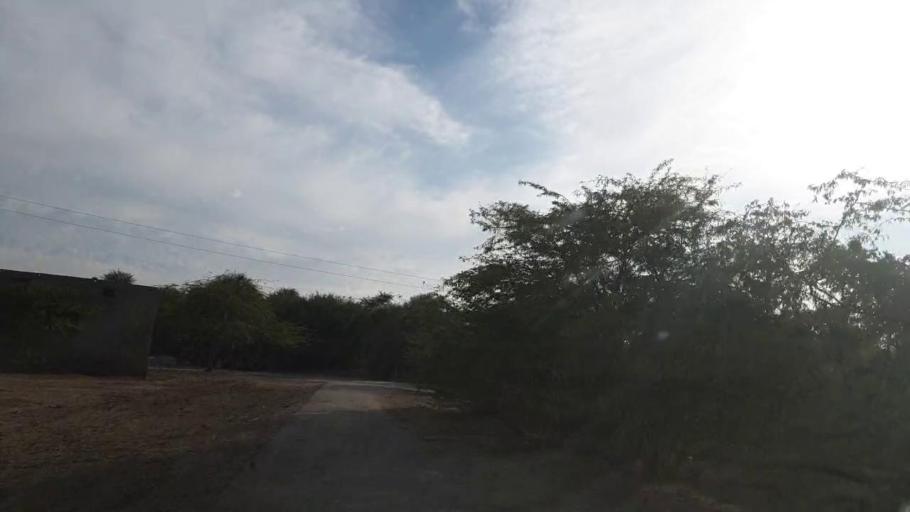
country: PK
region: Sindh
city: Pithoro
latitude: 25.6391
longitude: 69.3610
